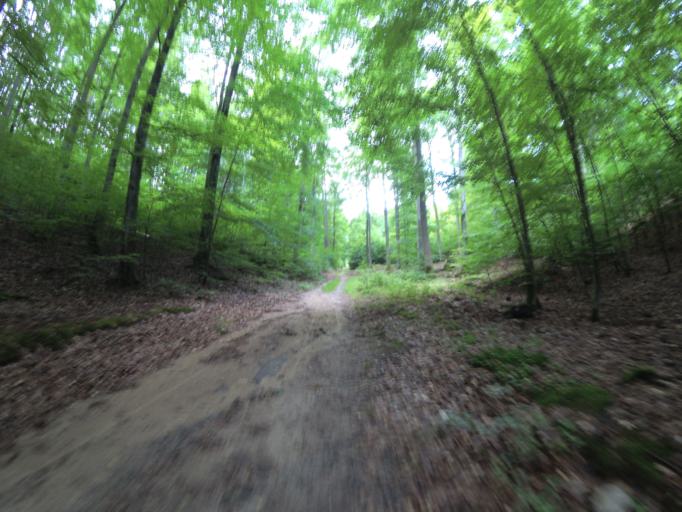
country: PL
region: Pomeranian Voivodeship
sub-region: Gdynia
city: Wielki Kack
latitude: 54.5084
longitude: 18.4423
